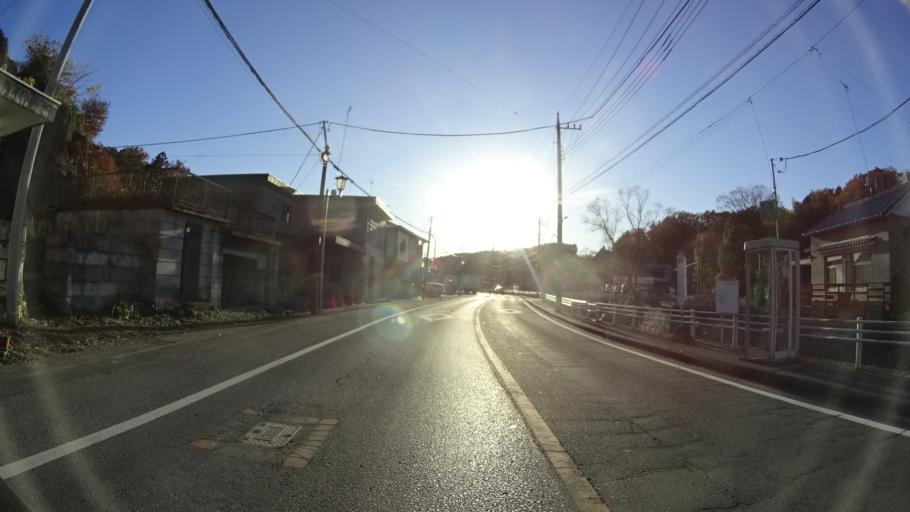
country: JP
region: Tochigi
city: Utsunomiya-shi
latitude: 36.5964
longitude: 139.8194
